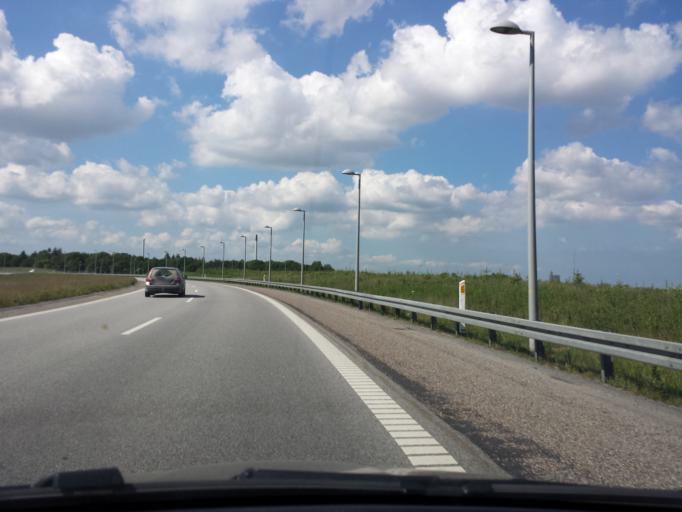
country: DK
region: Capital Region
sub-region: Rodovre Kommune
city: Rodovre
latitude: 55.6881
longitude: 12.4300
